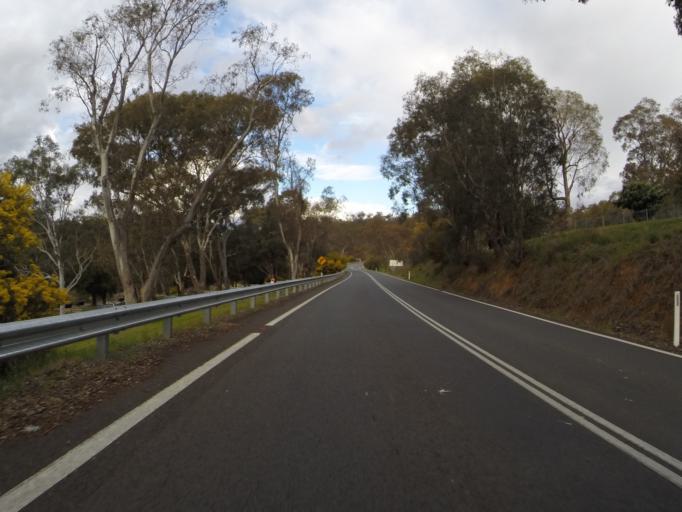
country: AU
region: Australian Capital Territory
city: Macquarie
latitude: -35.3204
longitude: 148.9531
